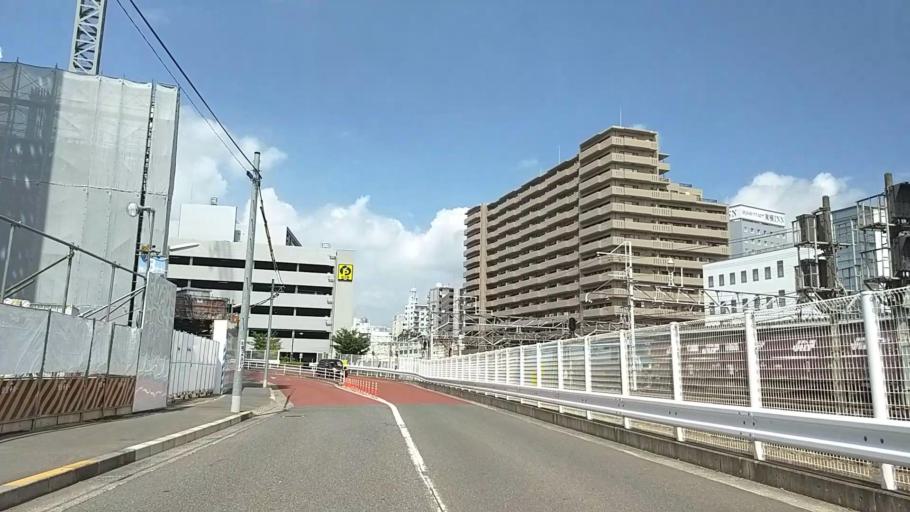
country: JP
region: Tokyo
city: Hachioji
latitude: 35.6552
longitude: 139.3382
